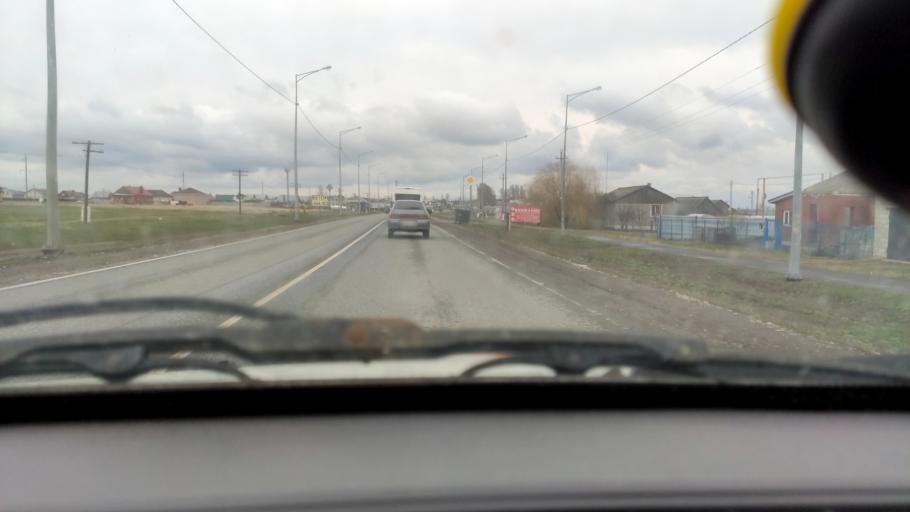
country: RU
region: Samara
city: Zhigulevsk
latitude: 53.5451
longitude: 49.5183
